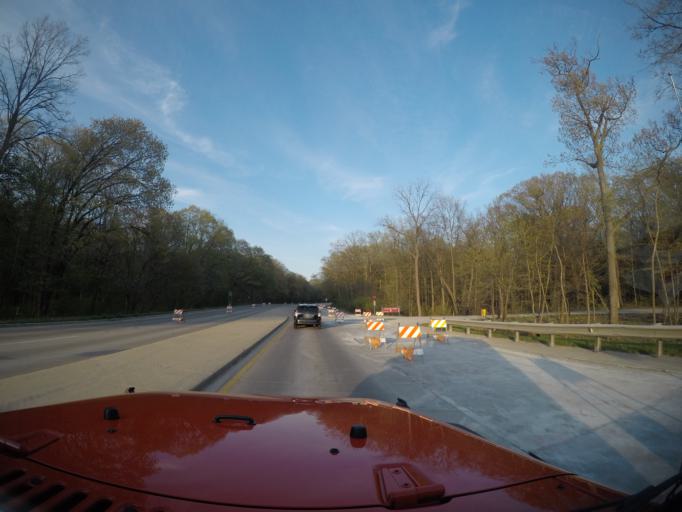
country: US
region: Illinois
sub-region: Cook County
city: Prospect Heights
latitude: 42.0876
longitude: -87.8862
